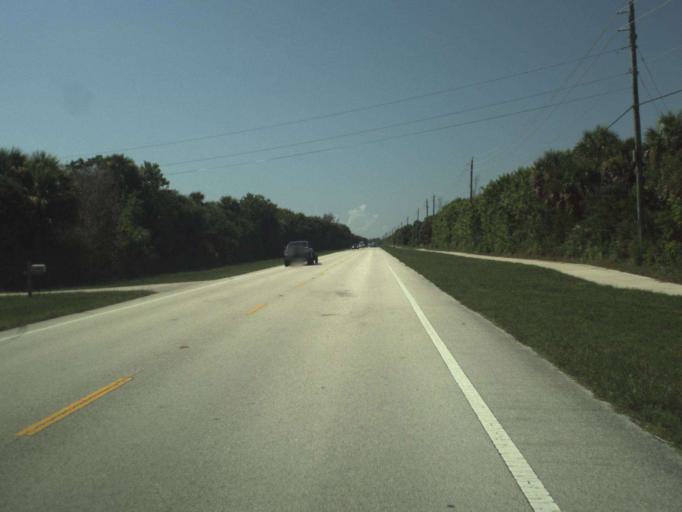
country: US
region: Florida
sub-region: Indian River County
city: Wabasso Beach
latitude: 27.8057
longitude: -80.4212
